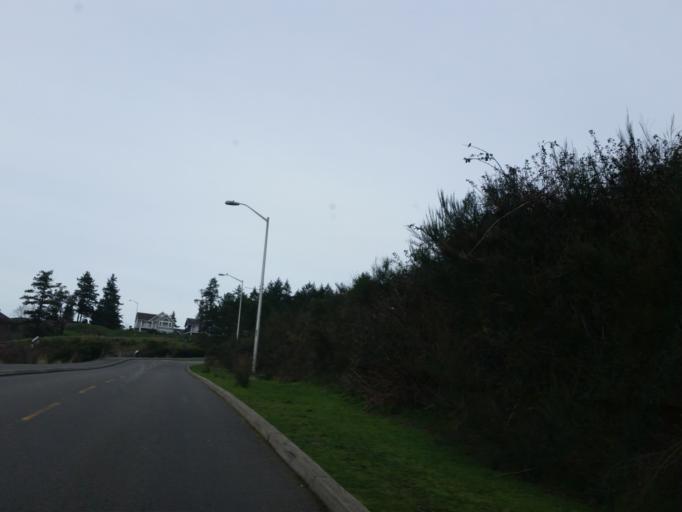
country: US
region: Washington
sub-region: Snohomish County
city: Woodway
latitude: 47.7648
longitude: -122.3829
